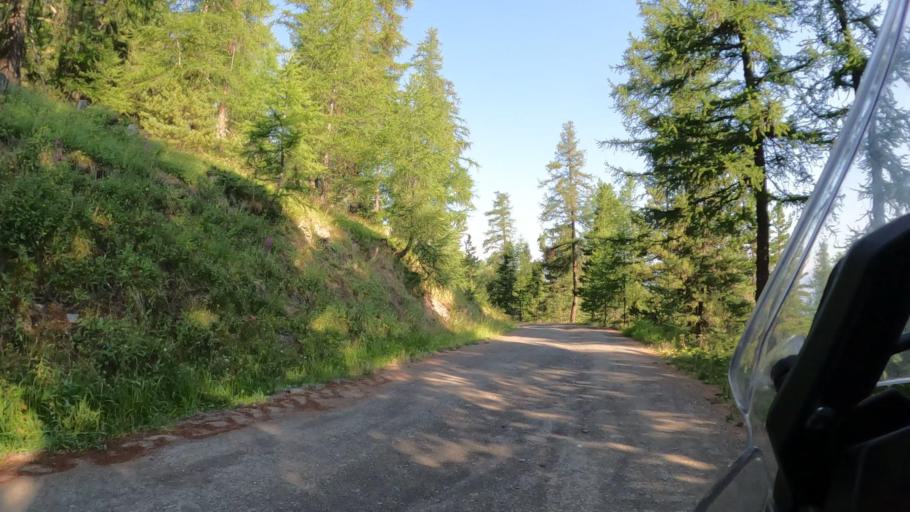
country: FR
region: Provence-Alpes-Cote d'Azur
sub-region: Departement des Hautes-Alpes
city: Guillestre
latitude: 44.6167
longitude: 6.6468
